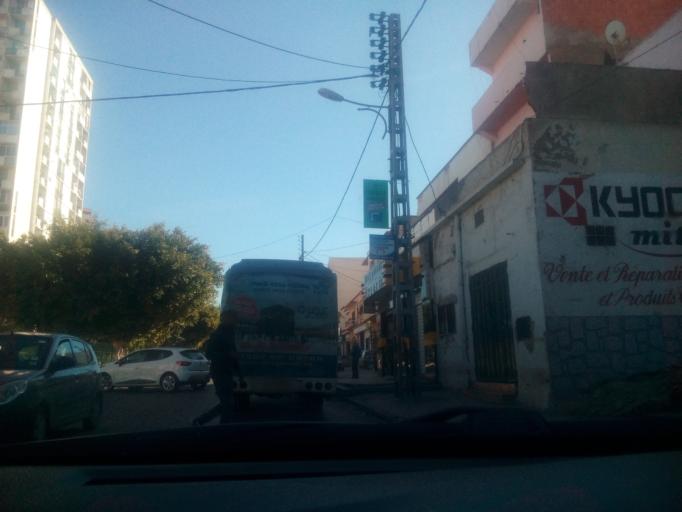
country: DZ
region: Oran
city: Oran
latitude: 35.7064
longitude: -0.6129
